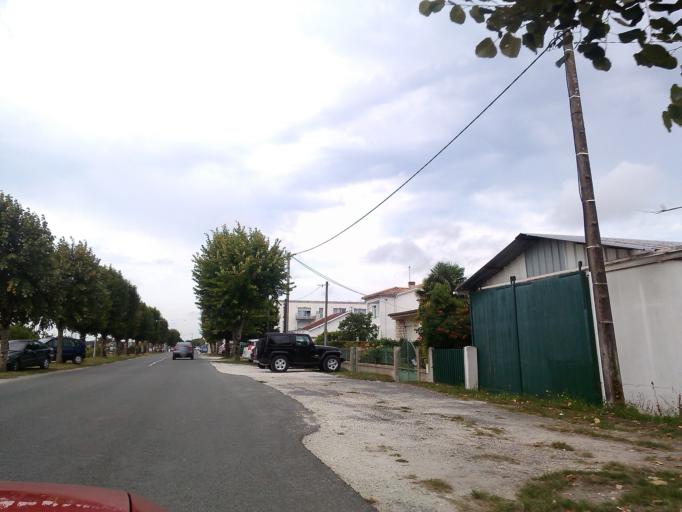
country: FR
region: Poitou-Charentes
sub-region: Departement de la Charente-Maritime
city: La Tremblade
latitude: 45.7695
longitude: -1.1341
